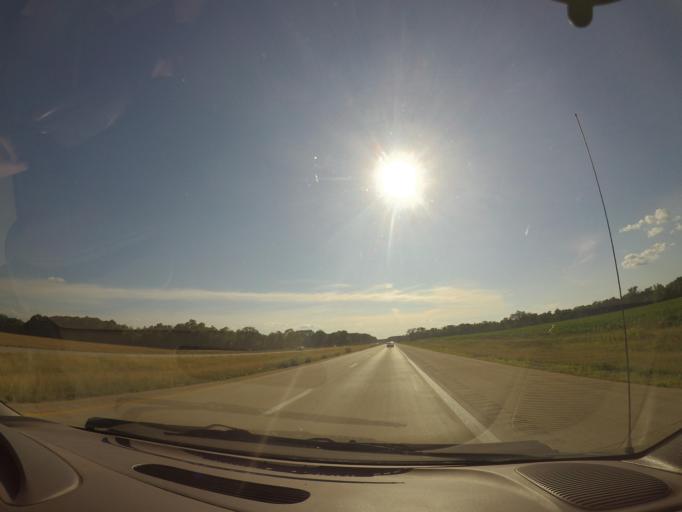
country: US
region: Ohio
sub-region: Henry County
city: Liberty Center
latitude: 41.4331
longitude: -83.9482
